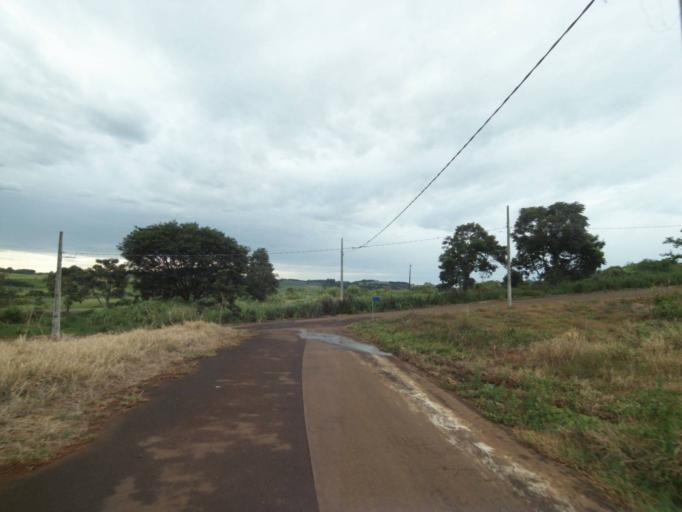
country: BR
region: Parana
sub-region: Guaraniacu
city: Guaraniacu
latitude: -25.1013
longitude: -52.8859
